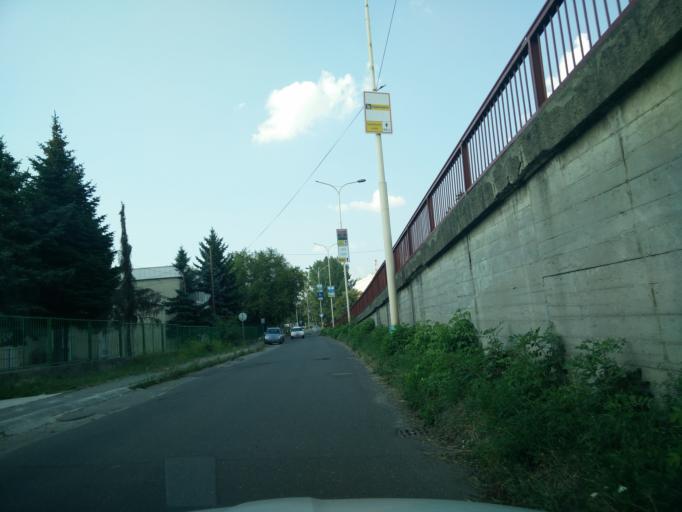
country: SK
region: Nitriansky
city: Prievidza
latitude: 48.7675
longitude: 18.6251
